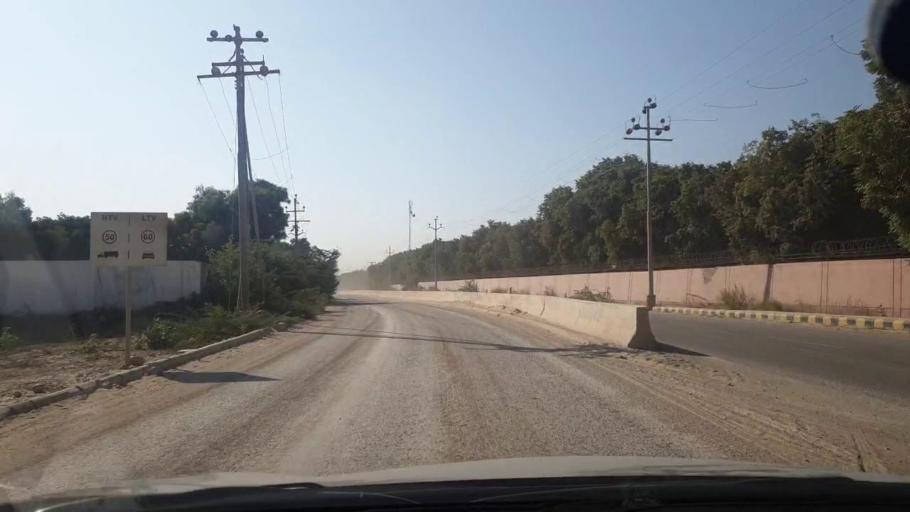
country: PK
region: Sindh
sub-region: Karachi District
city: Karachi
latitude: 25.0867
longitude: 67.0124
